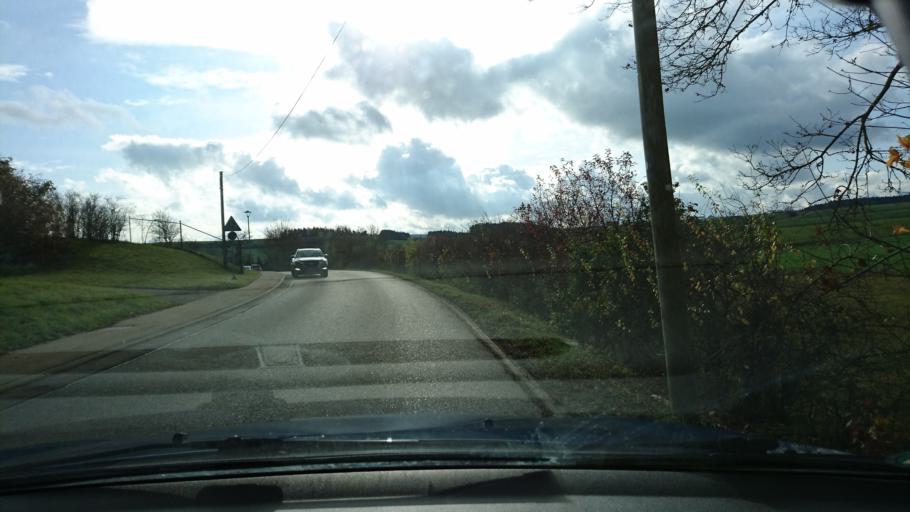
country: DE
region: Baden-Wuerttemberg
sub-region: Regierungsbezirk Stuttgart
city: Neresheim
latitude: 48.7566
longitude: 10.3180
